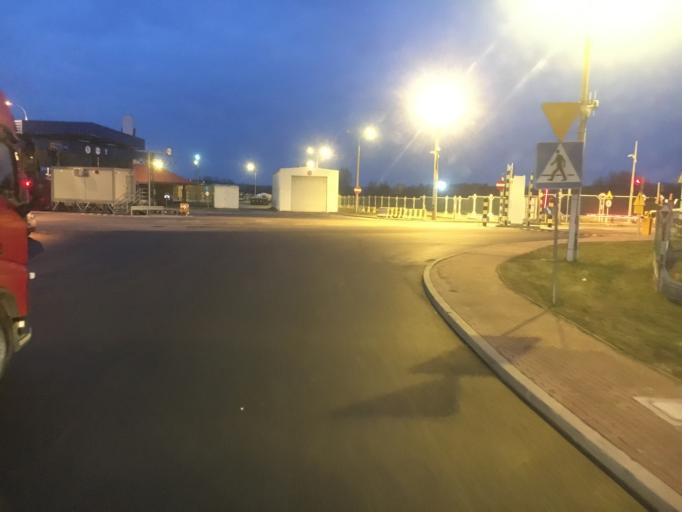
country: BY
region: Grodnenskaya
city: Vyalikaya Byerastavitsa
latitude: 53.1233
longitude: 23.8918
